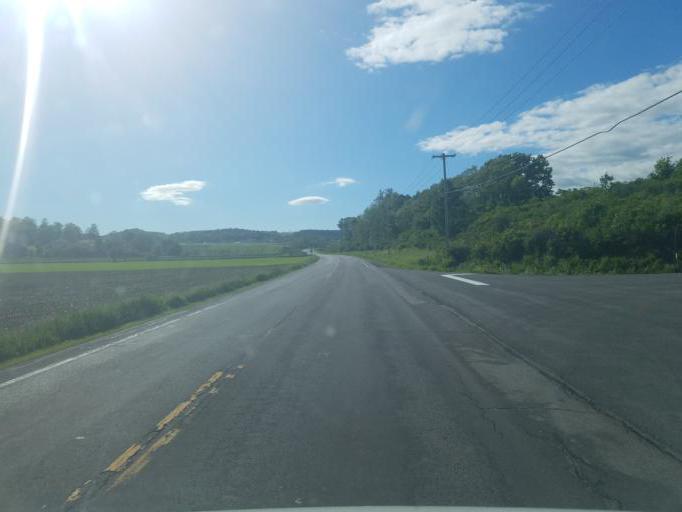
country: US
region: New York
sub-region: Herkimer County
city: Little Falls
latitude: 43.0140
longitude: -74.8041
